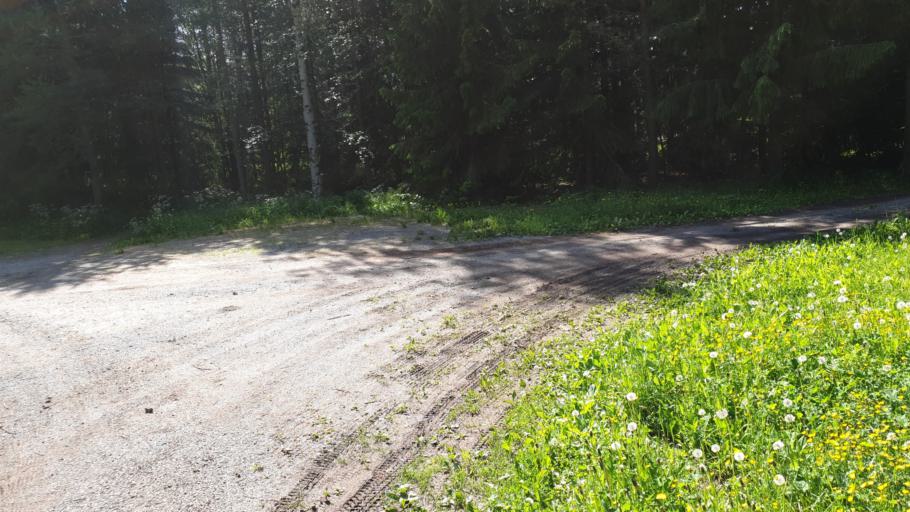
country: SE
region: Jaemtland
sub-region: OEstersunds Kommun
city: Ostersund
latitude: 63.1919
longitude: 14.6367
